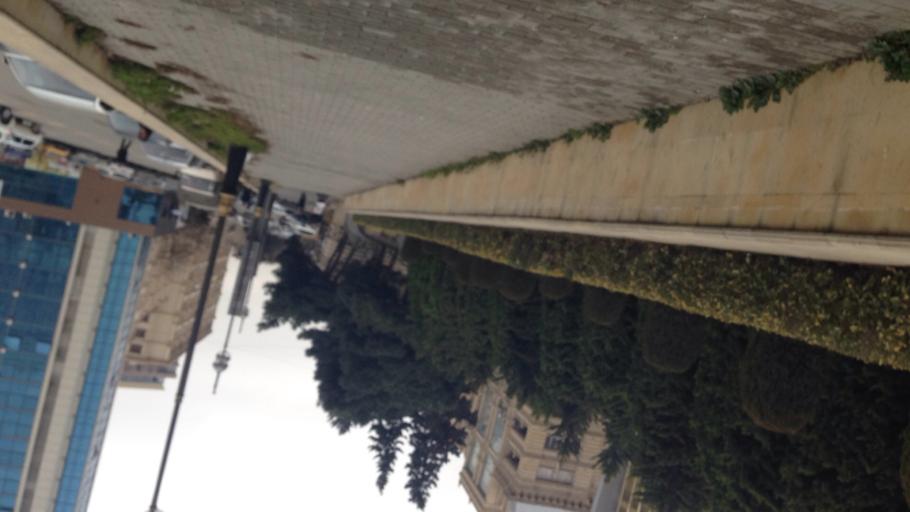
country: AZ
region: Baki
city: Badamdar
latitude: 40.3831
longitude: 49.8227
